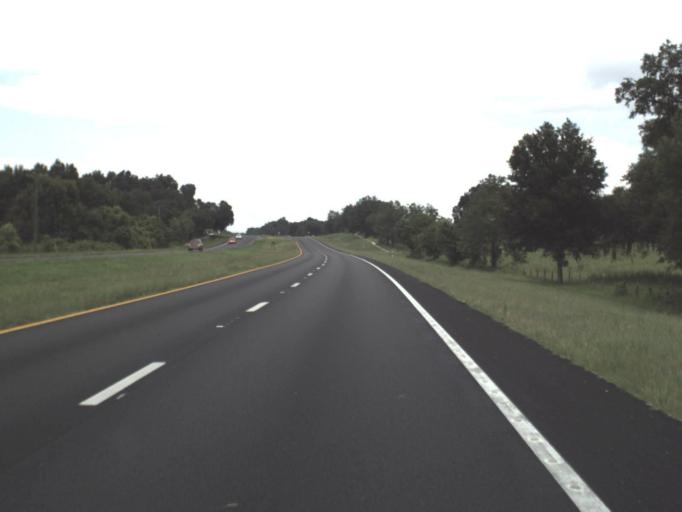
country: US
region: Florida
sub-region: Pasco County
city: Dade City North
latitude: 28.4159
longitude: -82.1906
